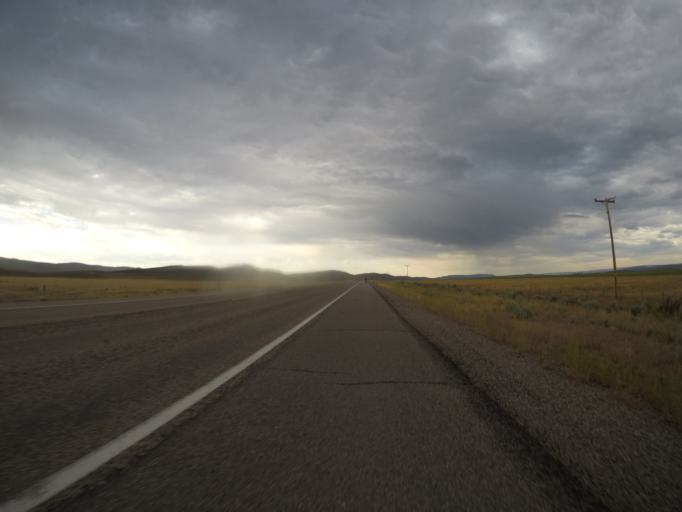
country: US
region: Utah
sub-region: Rich County
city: Randolph
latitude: 41.9183
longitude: -110.9550
